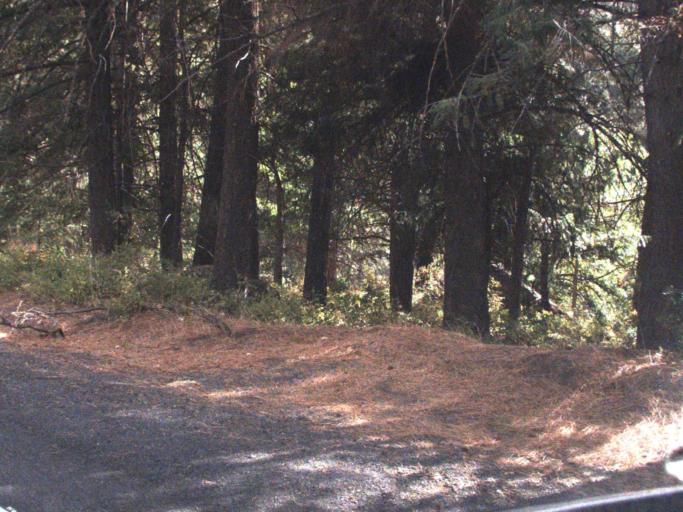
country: US
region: Washington
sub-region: Yakima County
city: Tieton
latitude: 46.6712
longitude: -120.9752
